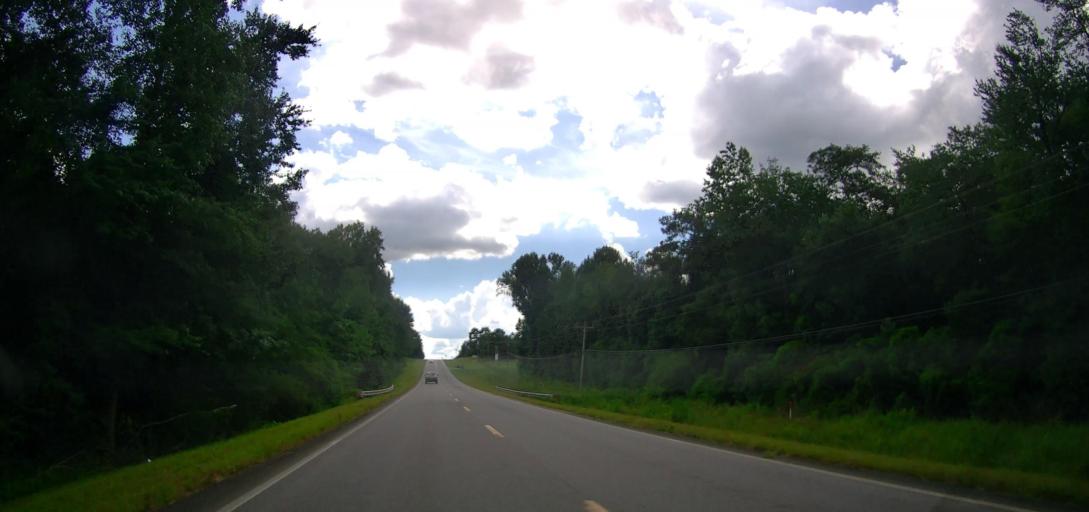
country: US
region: Alabama
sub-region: Russell County
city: Ladonia
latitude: 32.4449
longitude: -85.2732
